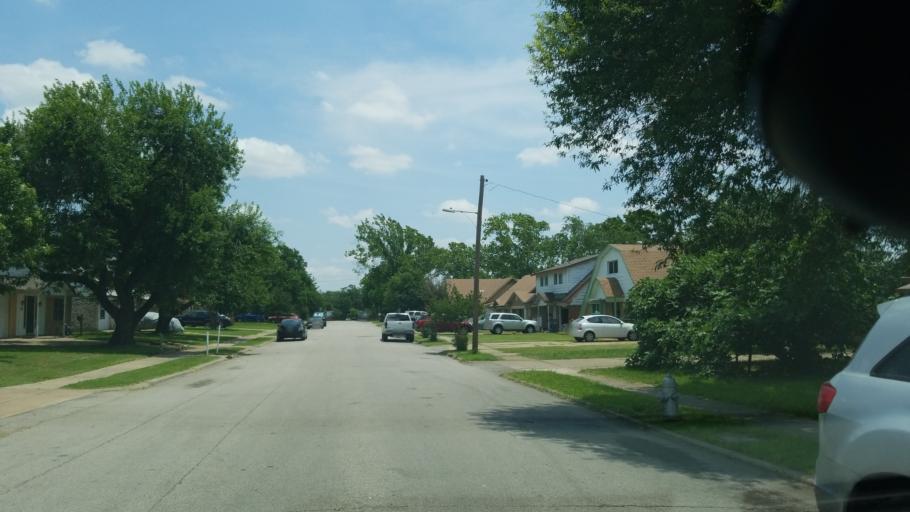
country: US
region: Texas
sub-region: Dallas County
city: Irving
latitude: 32.8412
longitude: -96.9534
